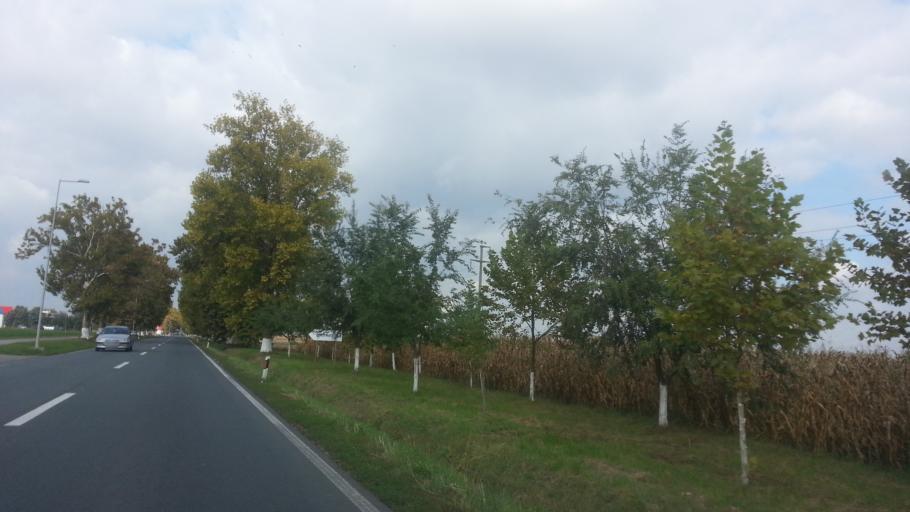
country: RS
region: Autonomna Pokrajina Vojvodina
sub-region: Sremski Okrug
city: Stara Pazova
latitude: 44.9663
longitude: 20.1848
